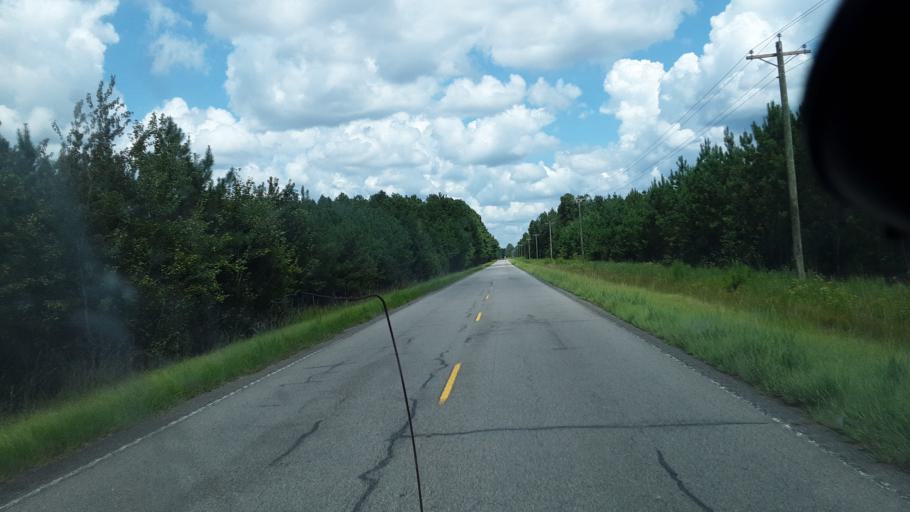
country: US
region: South Carolina
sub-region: Williamsburg County
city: Andrews
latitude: 33.5467
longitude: -79.4713
